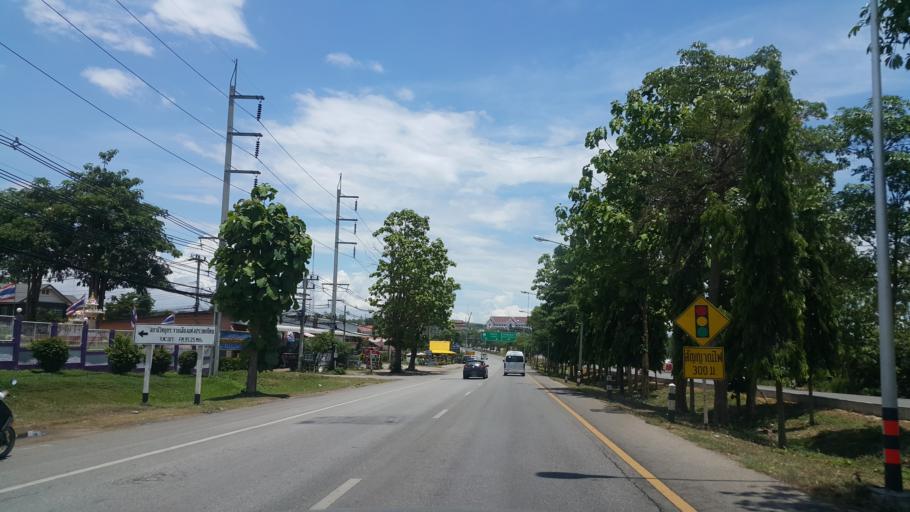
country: TH
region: Phayao
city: Phayao
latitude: 19.1989
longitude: 99.8738
